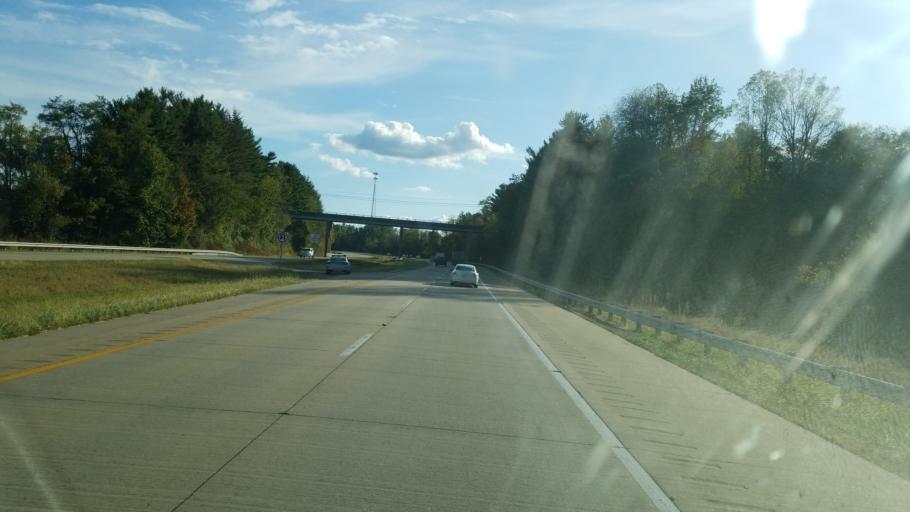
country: US
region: Ohio
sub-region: Washington County
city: Devola
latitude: 39.5140
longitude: -81.4533
